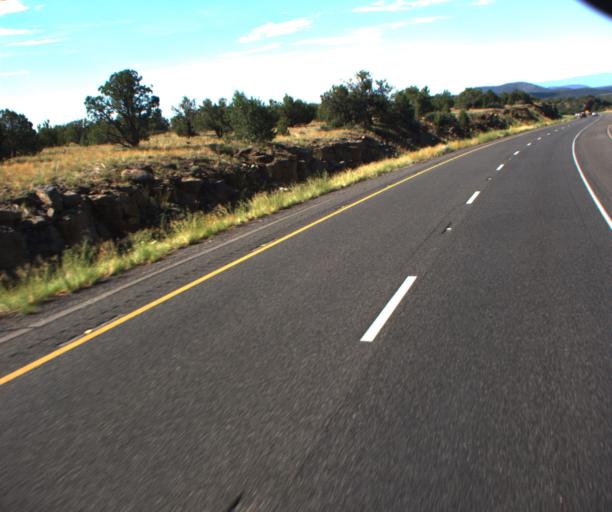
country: US
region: Arizona
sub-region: Yavapai County
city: Village of Oak Creek (Big Park)
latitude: 34.7984
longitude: -111.5988
